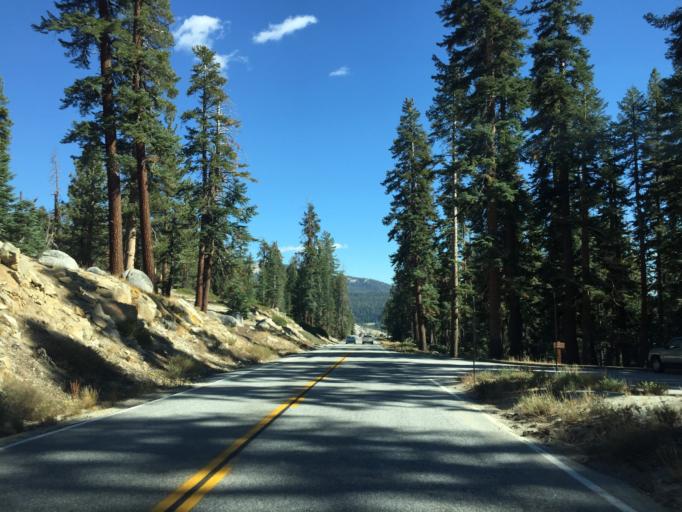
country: US
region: California
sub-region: Mariposa County
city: Yosemite Valley
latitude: 37.8503
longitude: -119.6148
